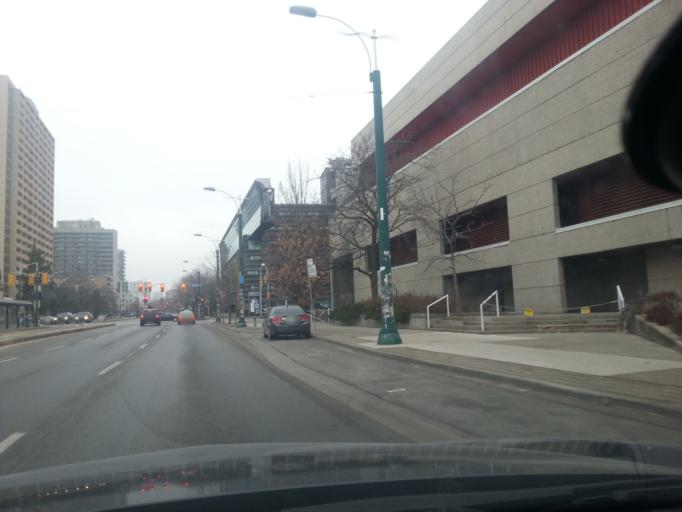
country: CA
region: Ontario
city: Toronto
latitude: 43.6624
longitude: -79.4017
